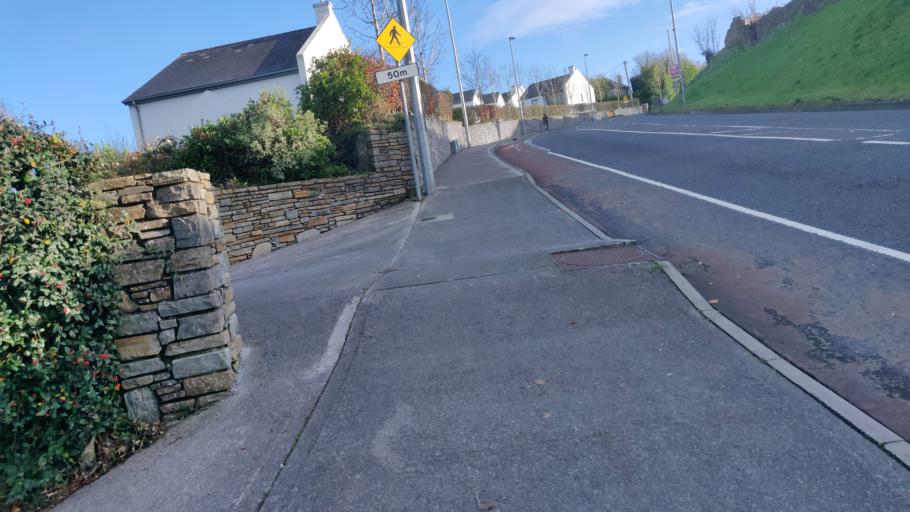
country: DE
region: North Rhine-Westphalia
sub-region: Regierungsbezirk Detmold
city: Guetersloh
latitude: 51.8721
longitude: 8.4207
